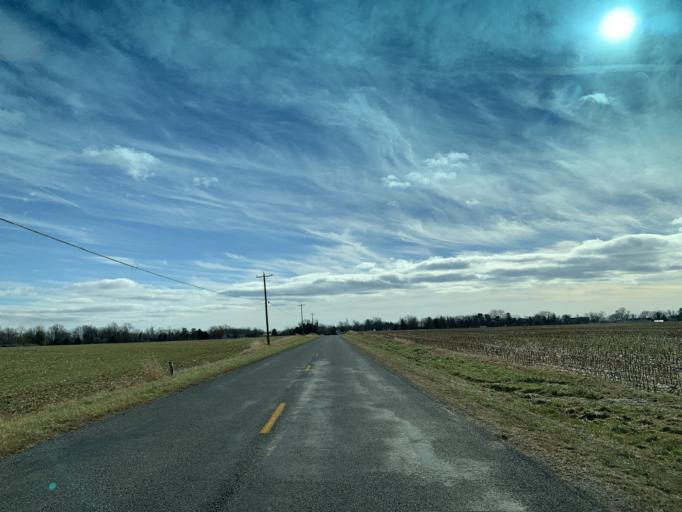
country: US
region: Maryland
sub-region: Kent County
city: Chestertown
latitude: 39.3348
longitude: -76.0463
